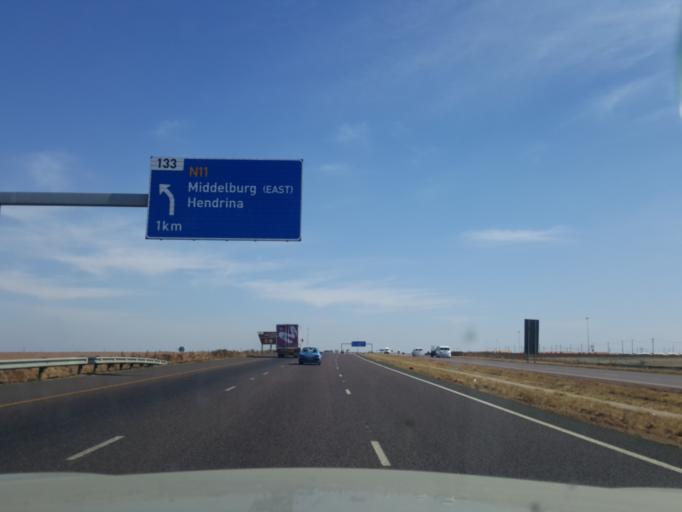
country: ZA
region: Mpumalanga
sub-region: Nkangala District Municipality
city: Middelburg
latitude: -25.8282
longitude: 29.5462
